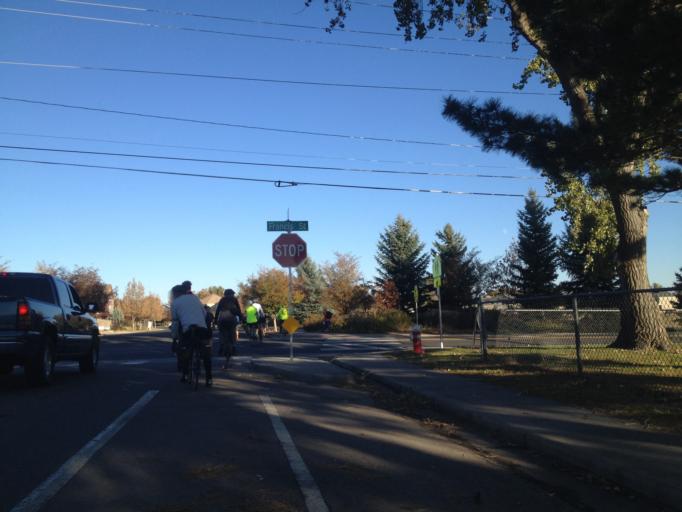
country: US
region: Colorado
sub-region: Boulder County
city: Longmont
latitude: 40.1849
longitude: -105.1170
